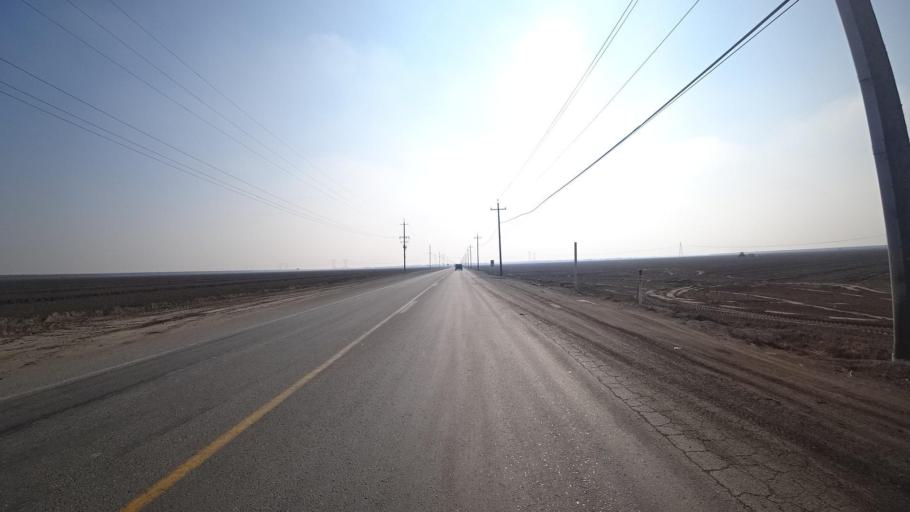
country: US
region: California
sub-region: Kern County
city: Greenfield
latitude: 35.2087
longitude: -119.1099
